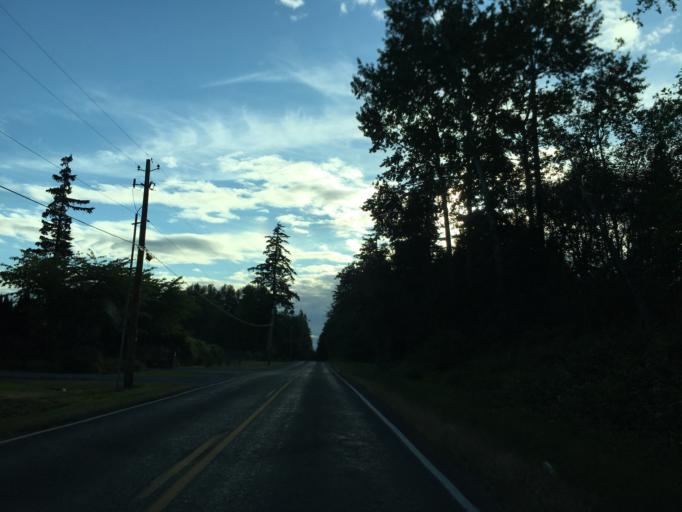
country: US
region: Washington
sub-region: Whatcom County
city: Birch Bay
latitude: 48.9405
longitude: -122.8086
